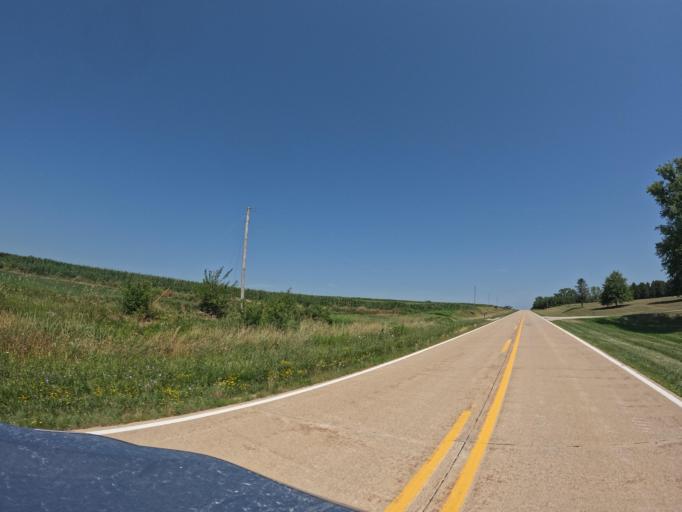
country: US
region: Iowa
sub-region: Henry County
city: Mount Pleasant
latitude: 40.8769
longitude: -91.5603
